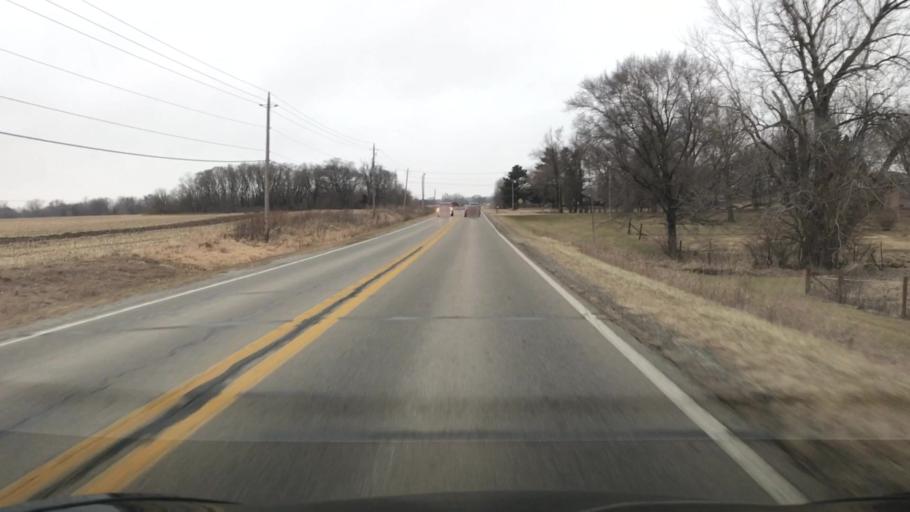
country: US
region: Iowa
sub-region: Polk County
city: Bondurant
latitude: 41.6755
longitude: -93.4645
